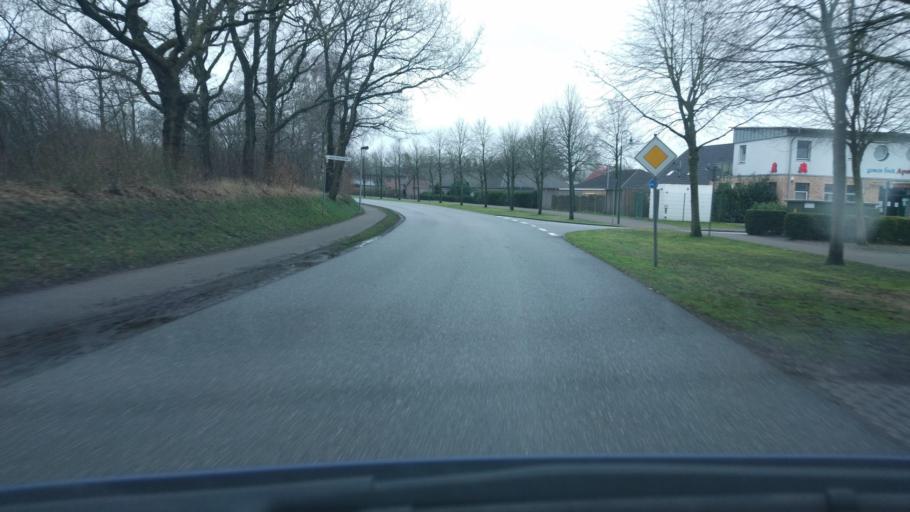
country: DE
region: Schleswig-Holstein
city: Kropp
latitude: 54.4133
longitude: 9.4955
